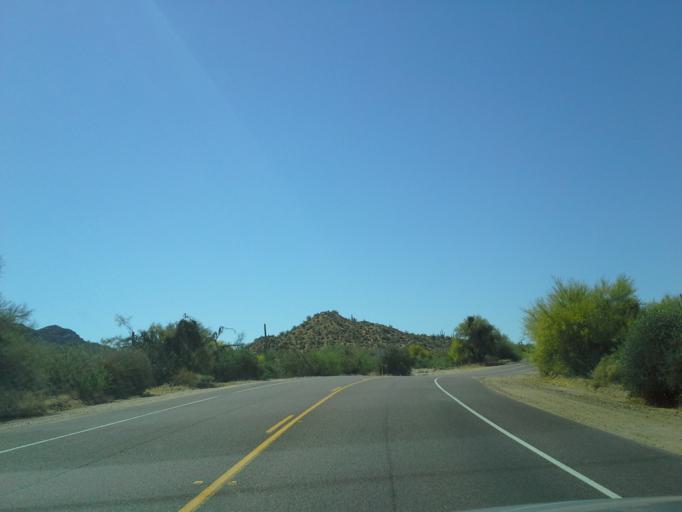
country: US
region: Arizona
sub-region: Pinal County
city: Apache Junction
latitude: 33.5083
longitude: -111.6175
